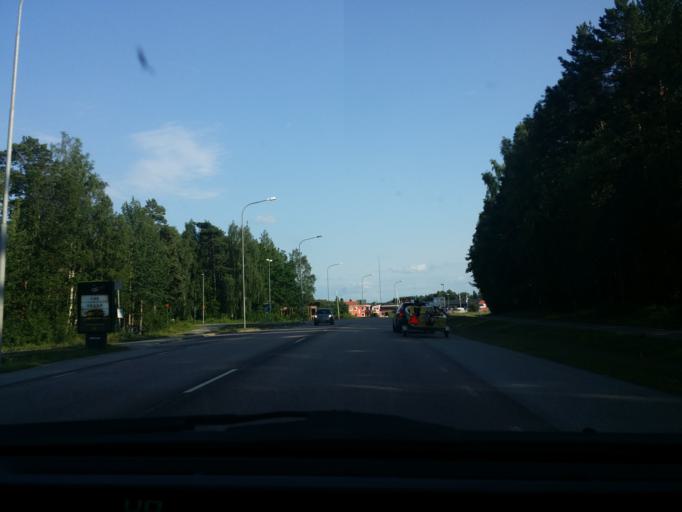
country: SE
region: Vaestmanland
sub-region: Vasteras
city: Vasteras
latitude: 59.6182
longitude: 16.6016
